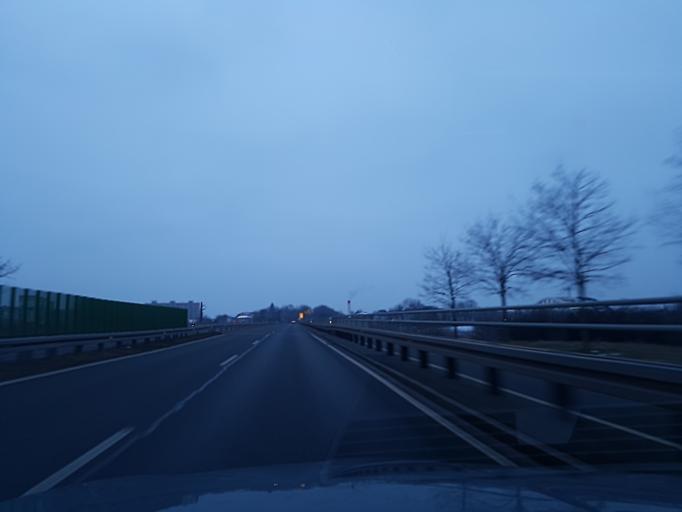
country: DE
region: Saxony
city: Riesa
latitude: 51.3126
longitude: 13.2983
